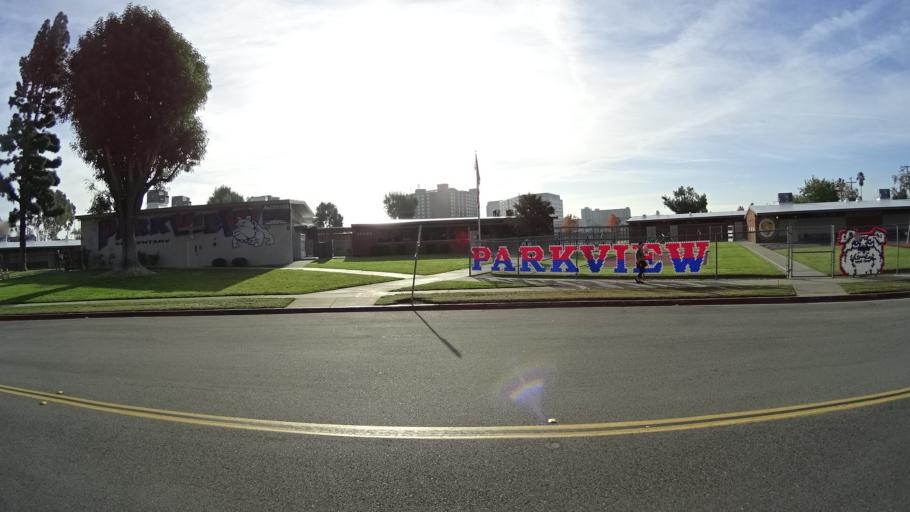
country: US
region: California
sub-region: Orange County
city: Garden Grove
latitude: 33.7939
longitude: -117.9190
